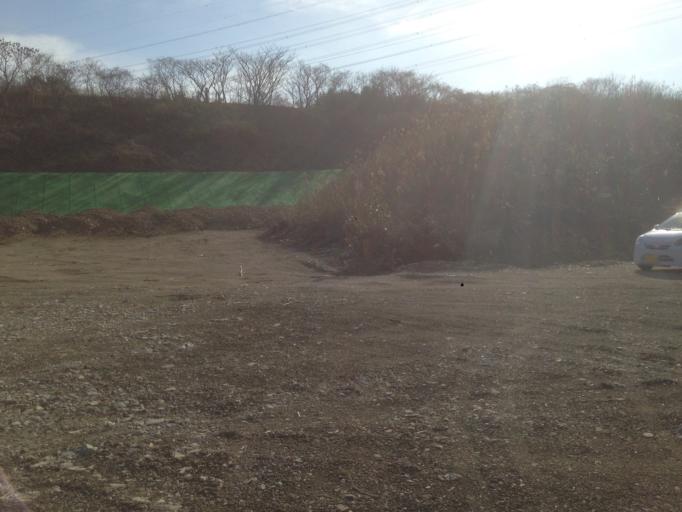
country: JP
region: Kanagawa
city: Yokosuka
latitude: 35.2450
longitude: 139.6432
